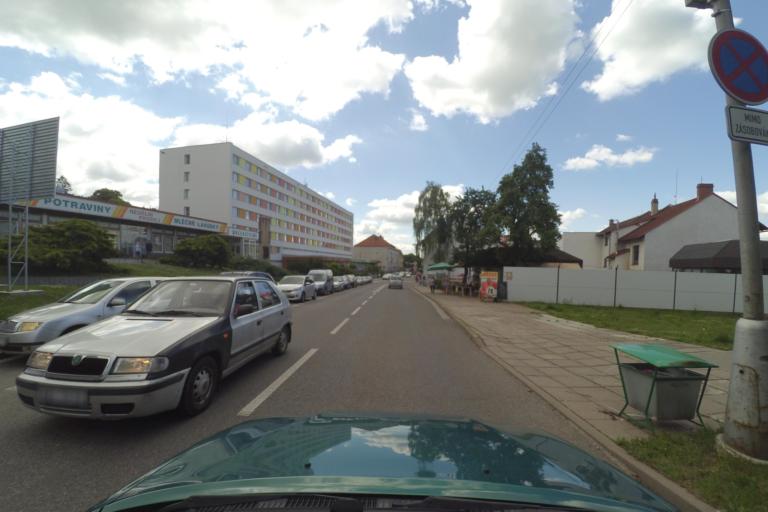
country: CZ
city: Nove Mesto nad Metuji
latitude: 50.3522
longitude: 16.1505
